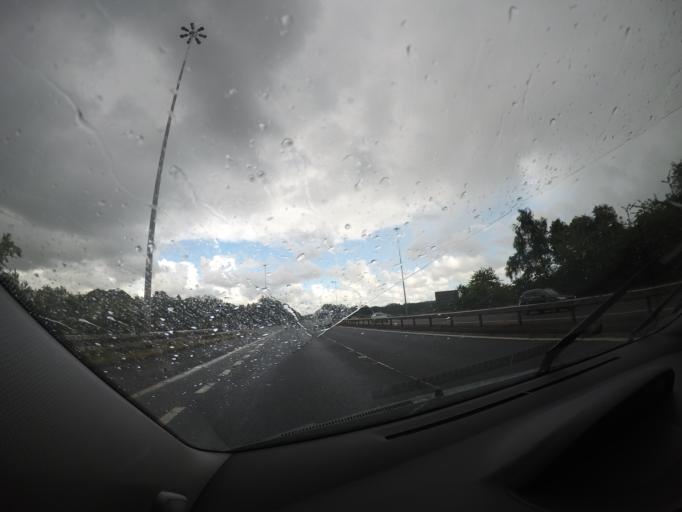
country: GB
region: Scotland
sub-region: South Lanarkshire
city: Hamilton
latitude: 55.7788
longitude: -4.0187
